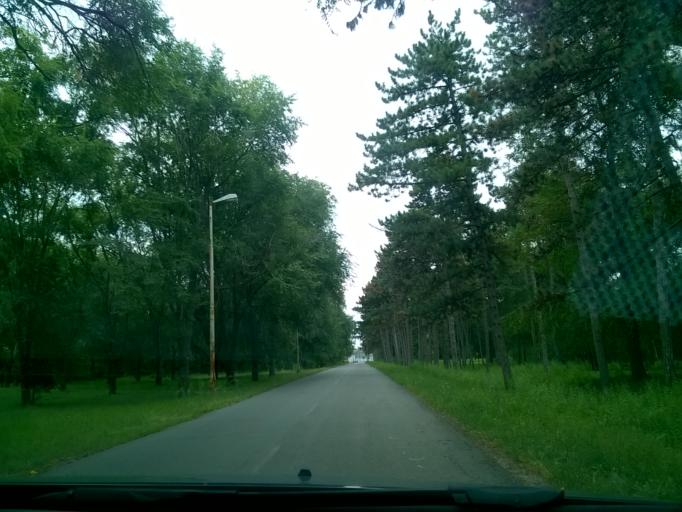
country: RS
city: Melenci
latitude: 45.5280
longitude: 20.3064
